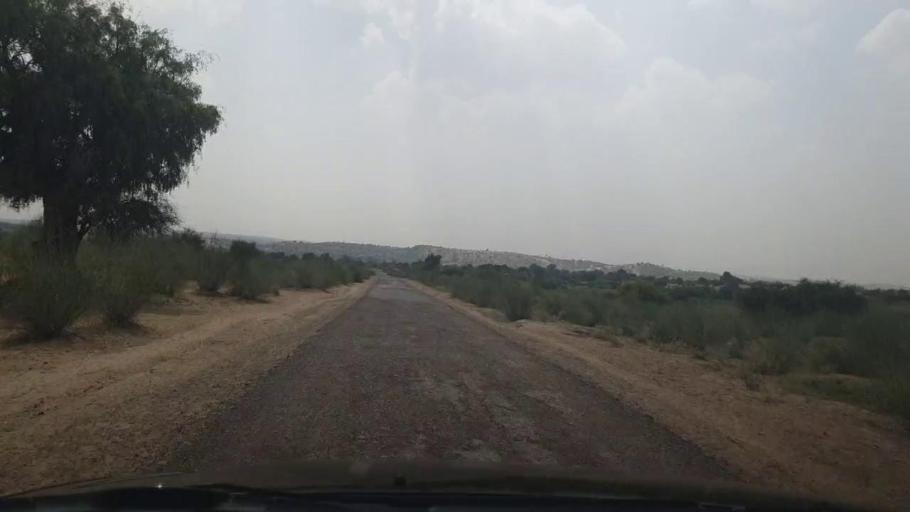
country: PK
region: Sindh
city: Islamkot
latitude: 25.0002
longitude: 70.4995
